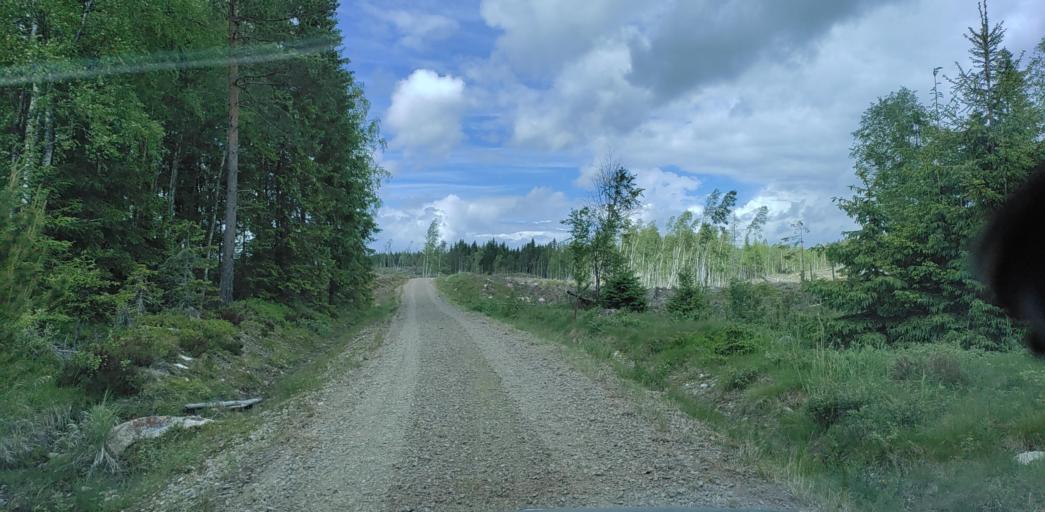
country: SE
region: Vaermland
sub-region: Munkfors Kommun
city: Munkfors
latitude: 59.9440
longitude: 13.4231
